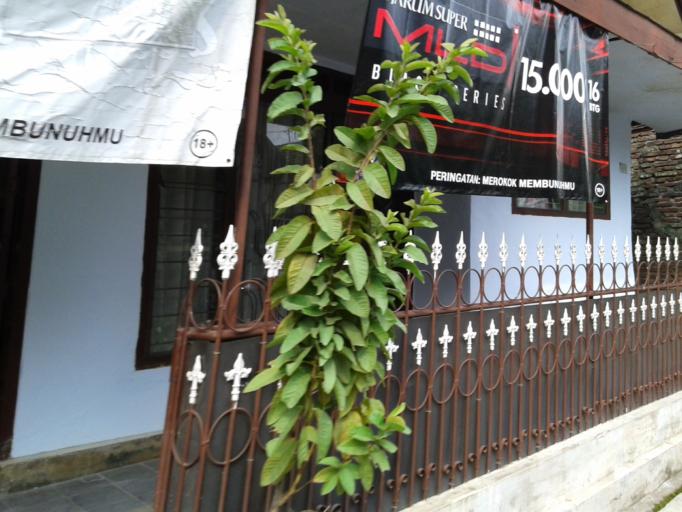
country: ID
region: East Java
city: Singosari
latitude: -7.9117
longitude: 112.6565
